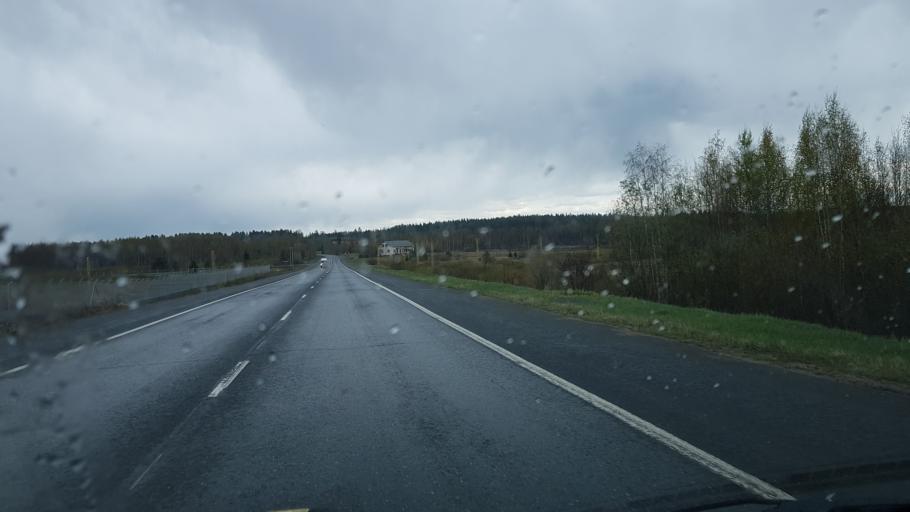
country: FI
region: Pirkanmaa
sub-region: Tampere
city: Pirkkala
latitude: 61.4189
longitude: 23.6344
